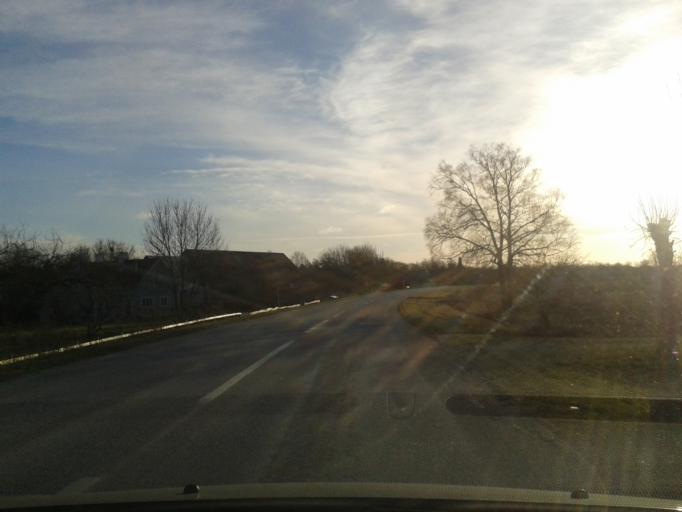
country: SE
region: Gotland
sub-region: Gotland
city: Hemse
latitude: 57.4278
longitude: 18.6318
